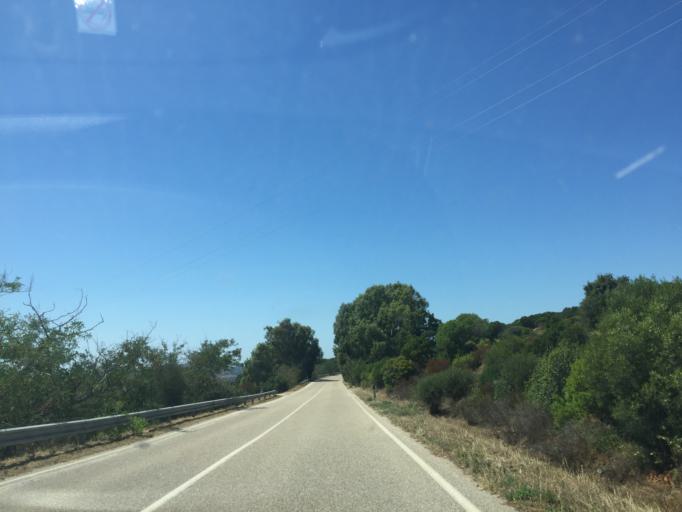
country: IT
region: Sardinia
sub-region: Provincia di Olbia-Tempio
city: Aglientu
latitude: 41.0982
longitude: 9.0876
